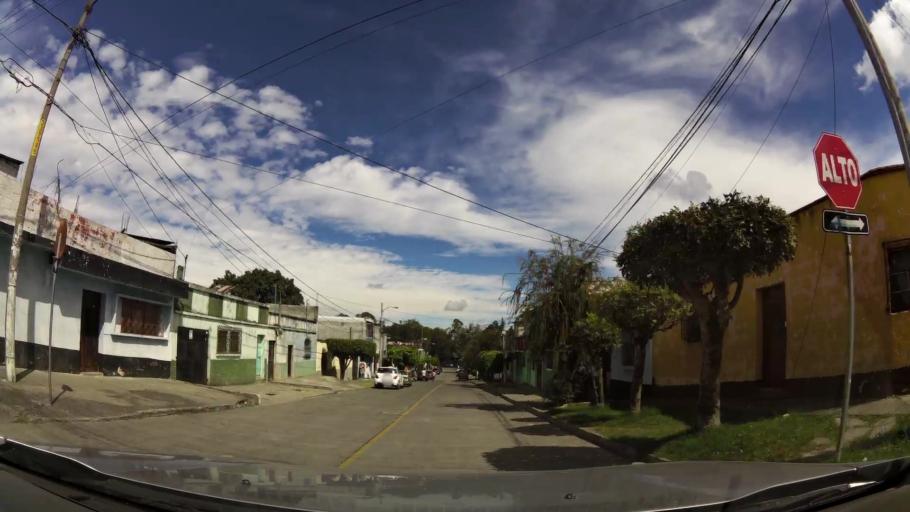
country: GT
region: Guatemala
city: Mixco
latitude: 14.6600
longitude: -90.5730
